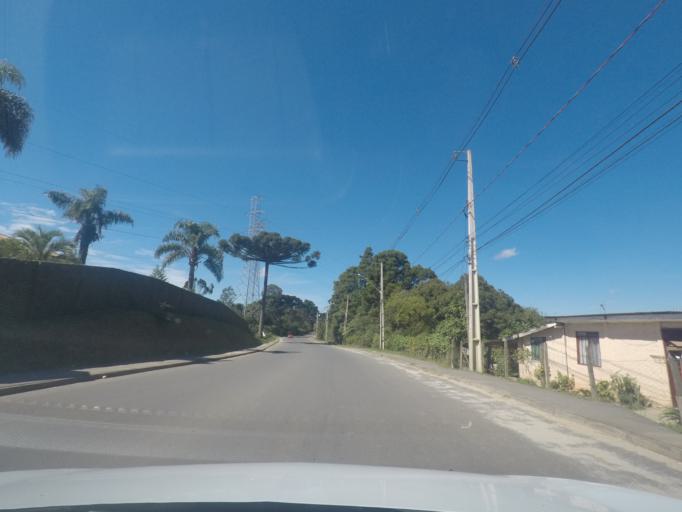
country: BR
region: Parana
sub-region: Almirante Tamandare
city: Almirante Tamandare
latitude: -25.3395
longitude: -49.3063
